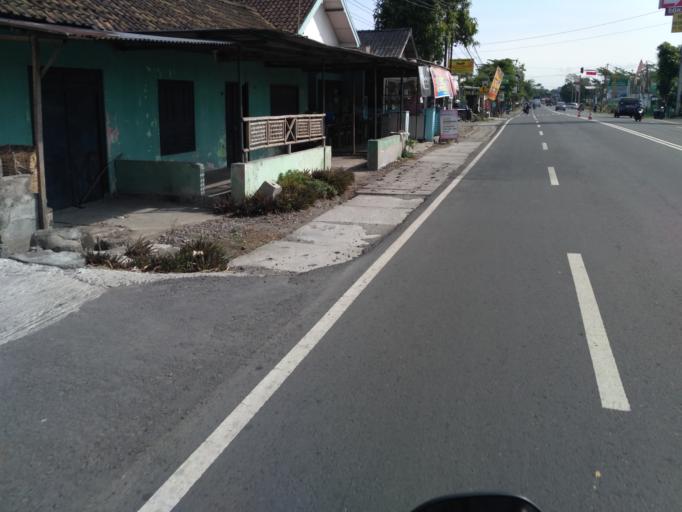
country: ID
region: Daerah Istimewa Yogyakarta
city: Godean
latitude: -7.8101
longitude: 110.2824
